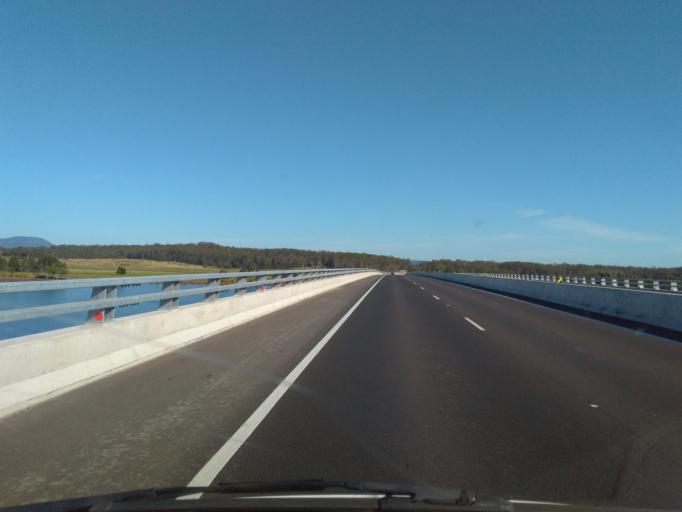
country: AU
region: New South Wales
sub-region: Port Macquarie-Hastings
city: North Shore
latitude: -31.4125
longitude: 152.8200
